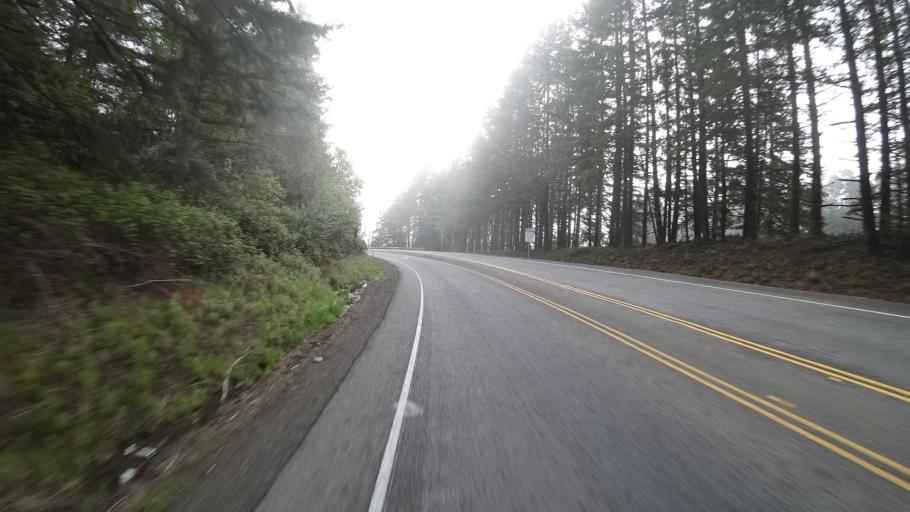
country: US
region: Oregon
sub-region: Coos County
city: Bunker Hill
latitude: 43.2891
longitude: -124.2223
